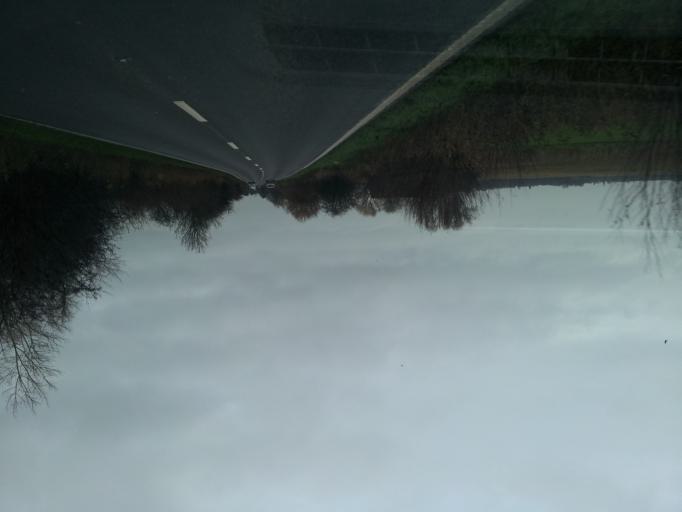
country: GB
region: England
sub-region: Norfolk
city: Acle
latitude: 52.6549
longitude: 1.5766
